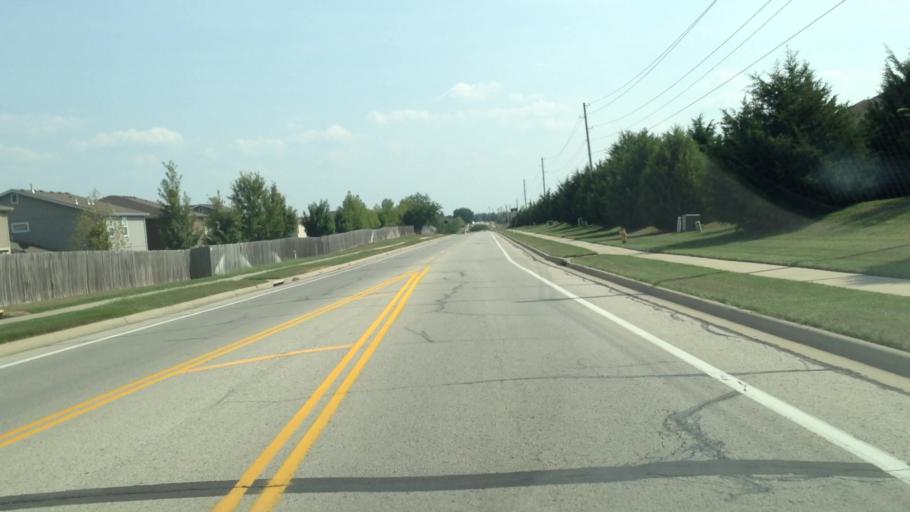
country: US
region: Kansas
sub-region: Douglas County
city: Lawrence
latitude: 38.9684
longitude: -95.3258
